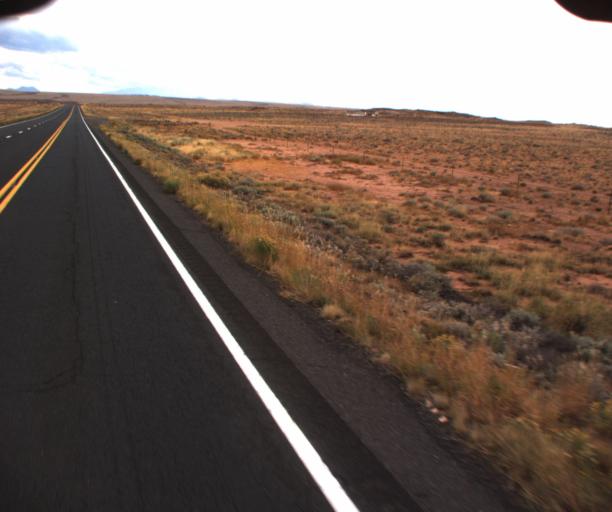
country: US
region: Arizona
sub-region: Coconino County
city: Tuba City
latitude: 35.8058
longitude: -111.4450
